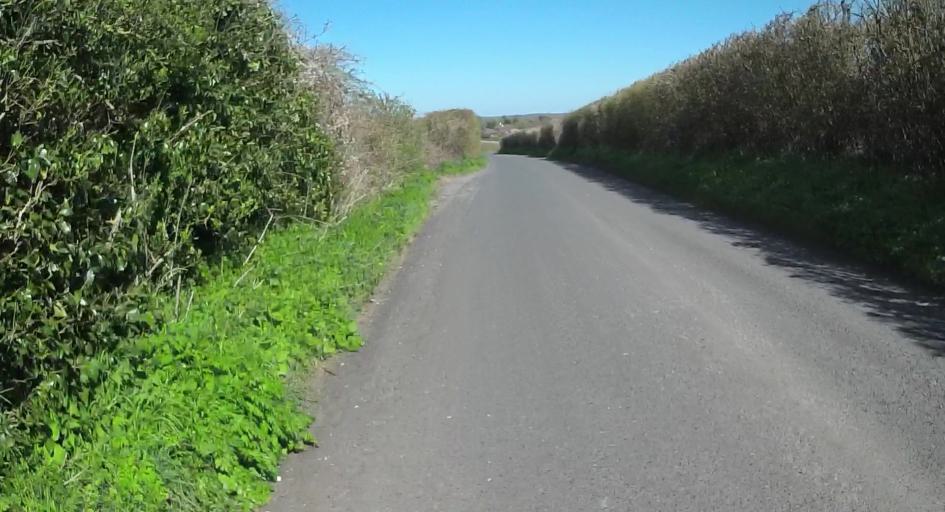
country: GB
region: England
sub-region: Hampshire
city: Hook
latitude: 51.2489
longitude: -0.9830
